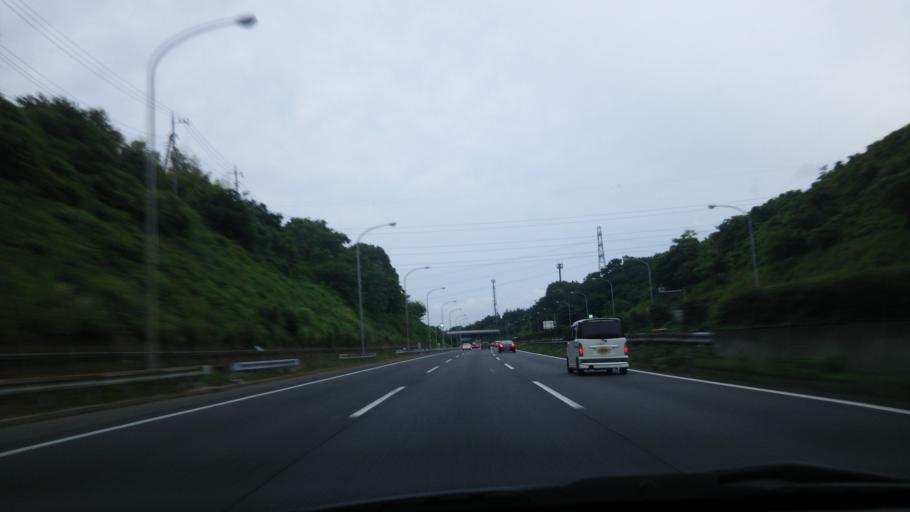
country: JP
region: Tokyo
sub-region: Machida-shi
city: Machida
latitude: 35.5143
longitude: 139.4911
